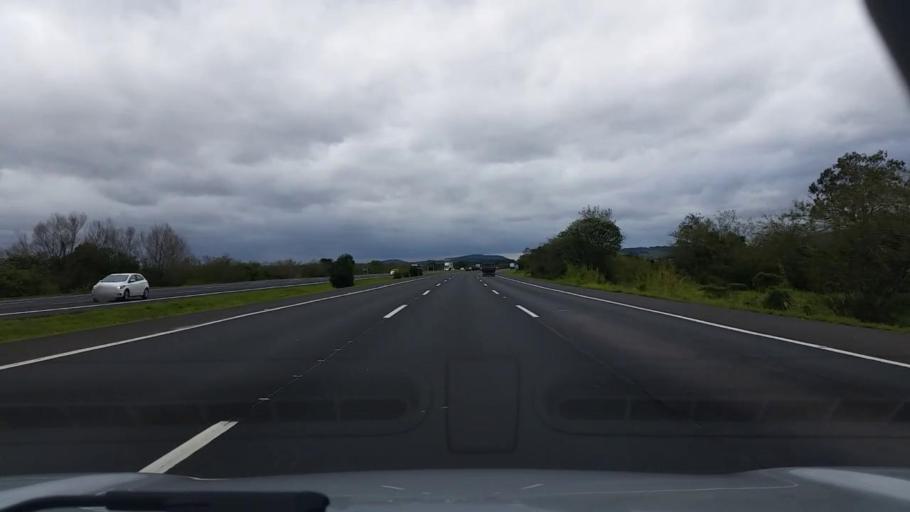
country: BR
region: Rio Grande do Sul
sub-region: Osorio
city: Osorio
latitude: -29.8789
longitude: -50.4311
